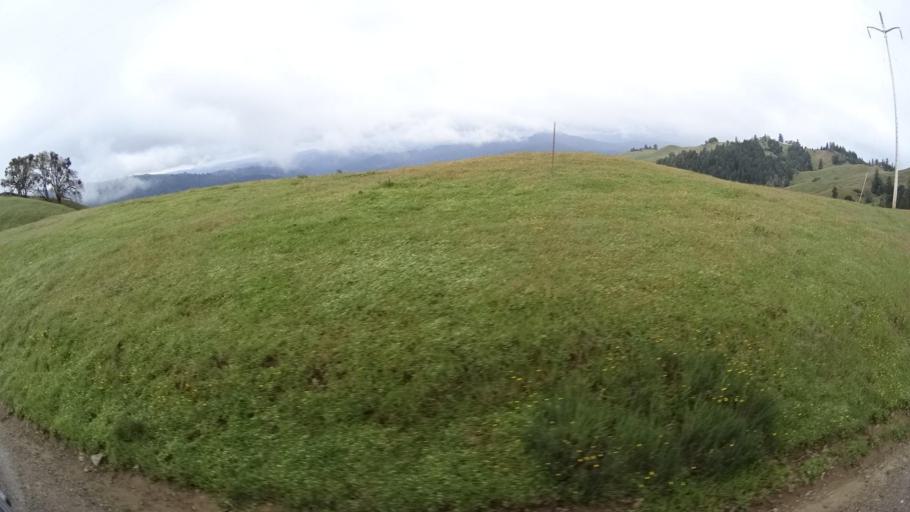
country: US
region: California
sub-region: Humboldt County
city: Redway
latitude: 40.2084
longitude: -123.7302
